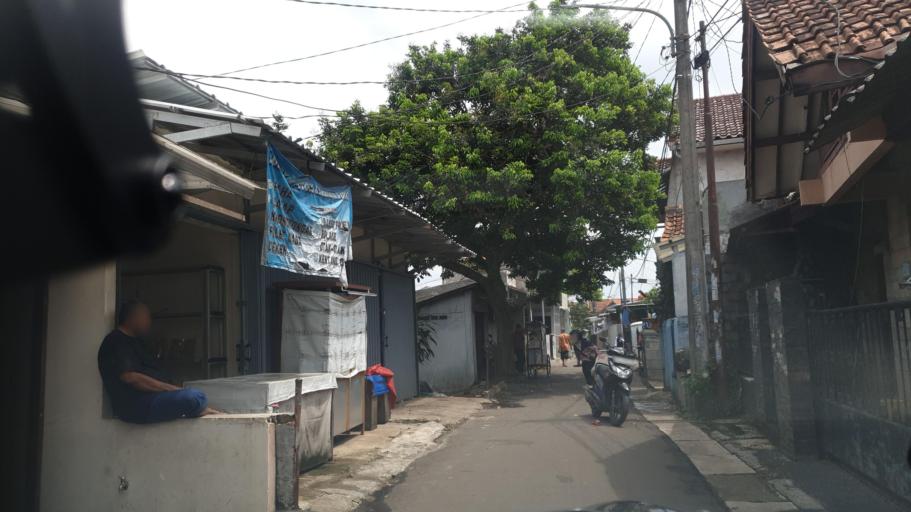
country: ID
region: West Java
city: Pamulang
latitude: -6.3368
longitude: 106.7686
